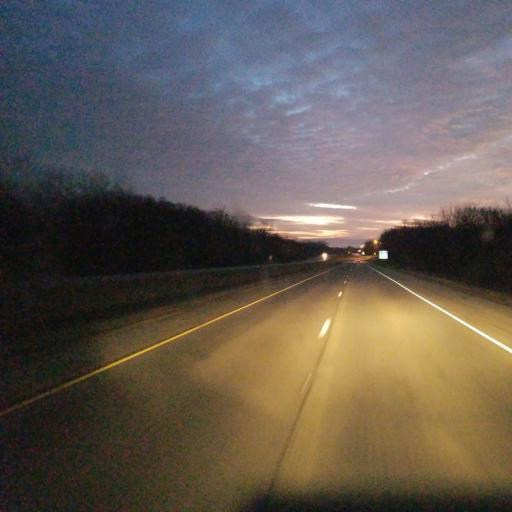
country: US
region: Illinois
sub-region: Peoria County
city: Bellevue
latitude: 40.6939
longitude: -89.6868
